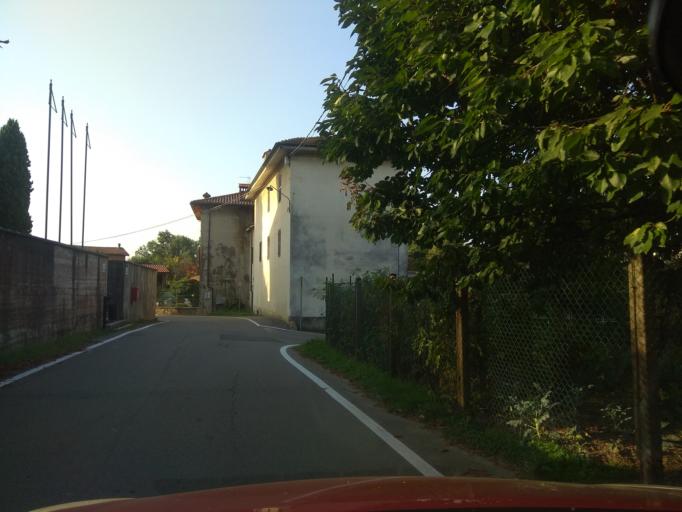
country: IT
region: Piedmont
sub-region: Provincia di Vercelli
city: San Maurizio
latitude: 45.6099
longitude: 8.3023
